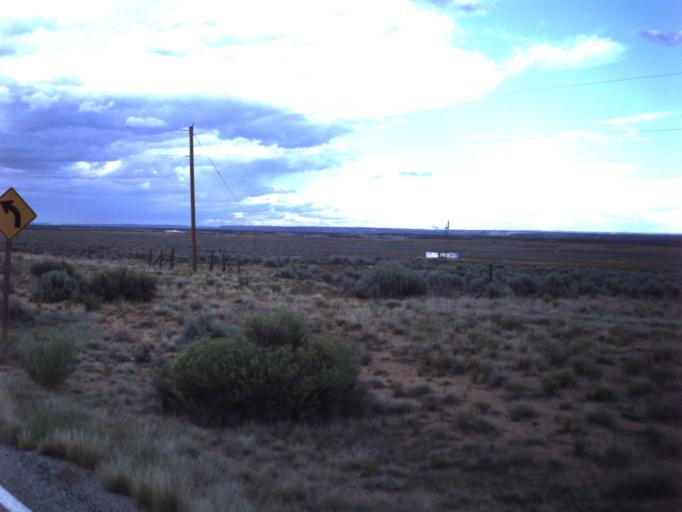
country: US
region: Utah
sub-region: San Juan County
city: Blanding
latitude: 37.4167
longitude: -109.3343
